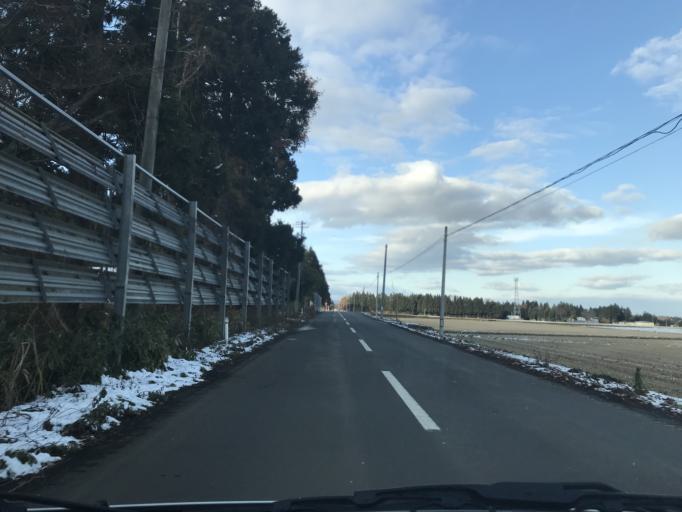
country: JP
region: Iwate
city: Kitakami
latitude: 39.2477
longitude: 141.0326
